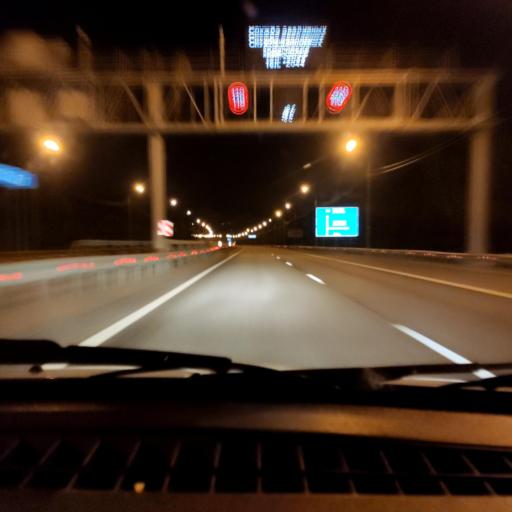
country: RU
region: Lipetsk
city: Zadonsk
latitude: 52.3649
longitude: 38.9291
